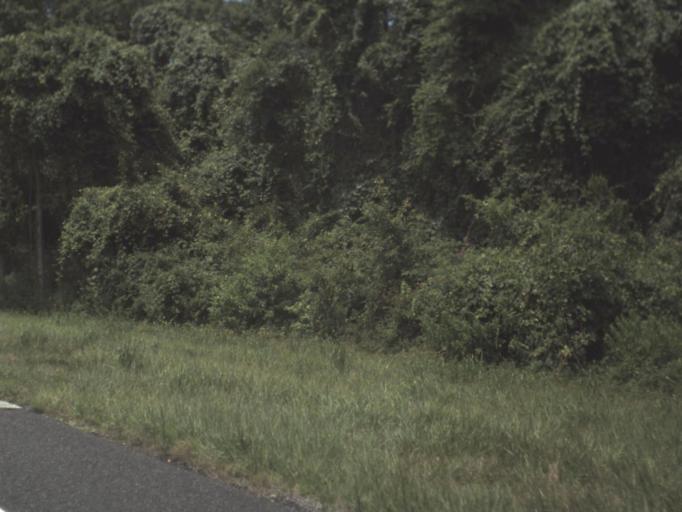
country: US
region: Florida
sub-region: Taylor County
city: Perry
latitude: 30.2478
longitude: -83.6977
